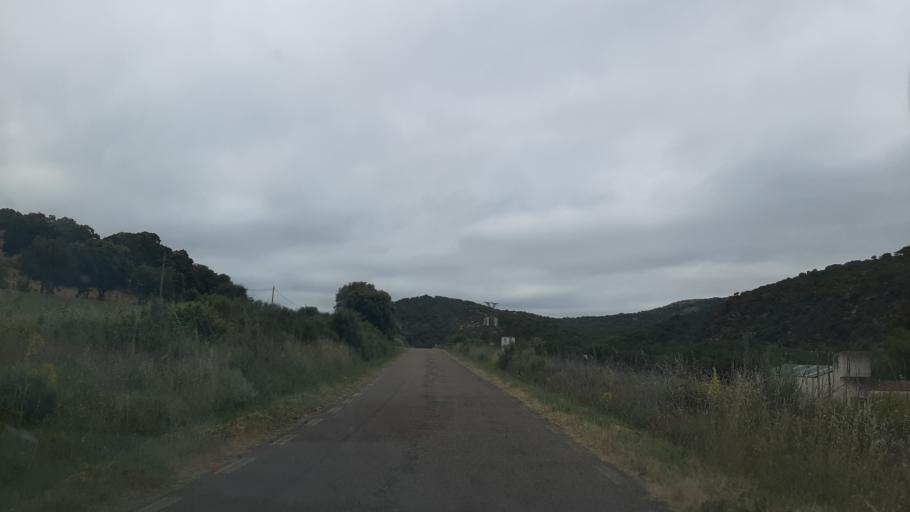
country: ES
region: Castille and Leon
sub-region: Provincia de Salamanca
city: Pastores
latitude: 40.5481
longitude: -6.4895
